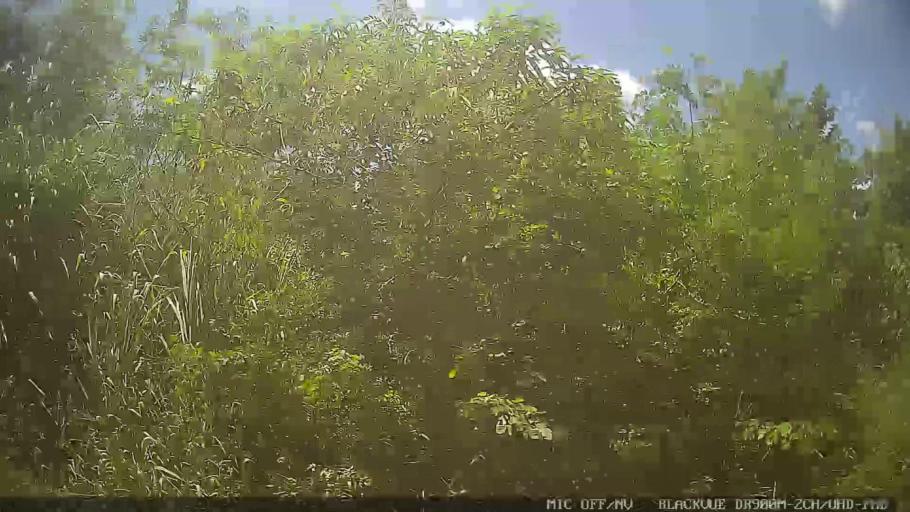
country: BR
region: Sao Paulo
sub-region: Braganca Paulista
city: Braganca Paulista
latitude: -23.0254
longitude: -46.5357
